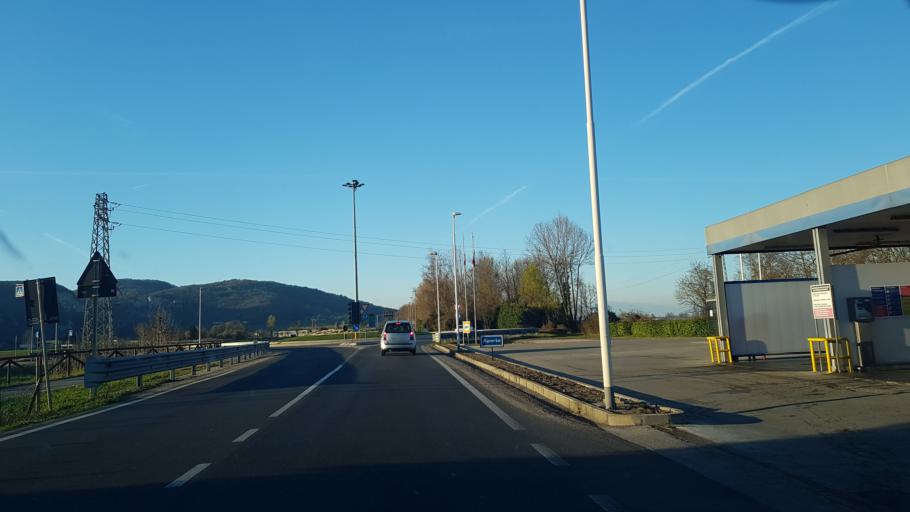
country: IT
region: Veneto
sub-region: Provincia di Vicenza
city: Ponte di Castegnero
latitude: 45.4420
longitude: 11.6009
